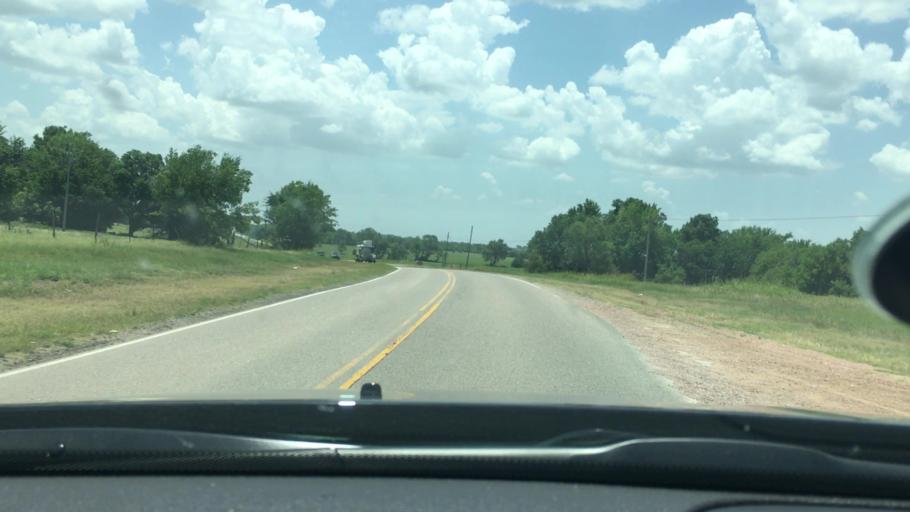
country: US
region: Oklahoma
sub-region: Johnston County
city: Tishomingo
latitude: 34.4720
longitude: -96.6357
